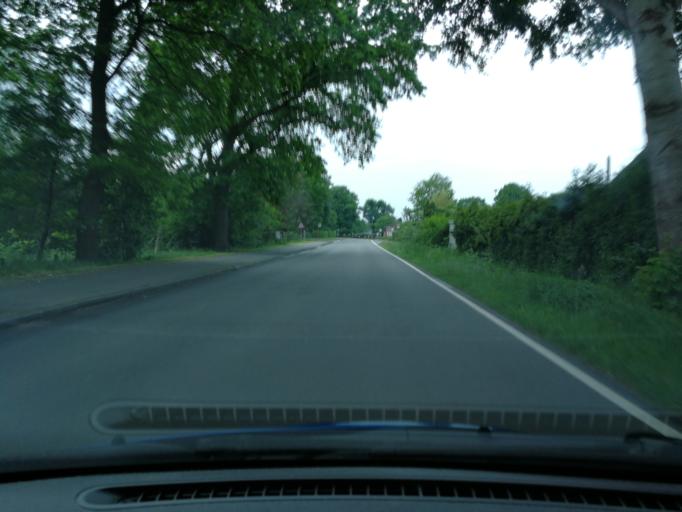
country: DE
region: Schleswig-Holstein
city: Roseburg
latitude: 53.5338
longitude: 10.6287
